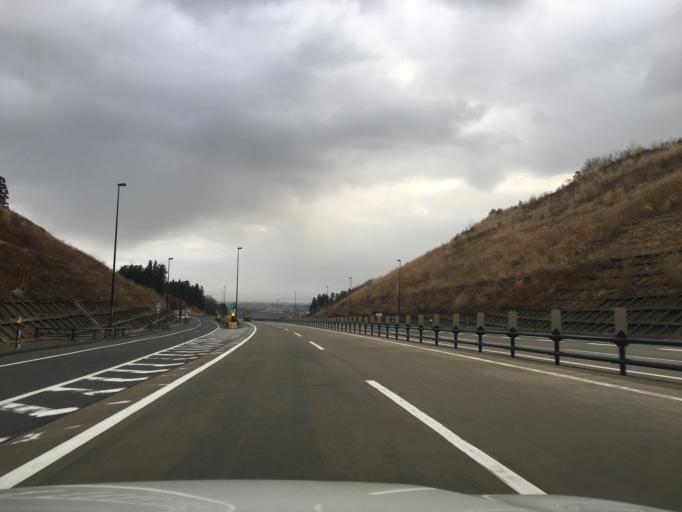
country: JP
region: Yamagata
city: Tsuruoka
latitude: 38.7005
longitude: 139.7176
